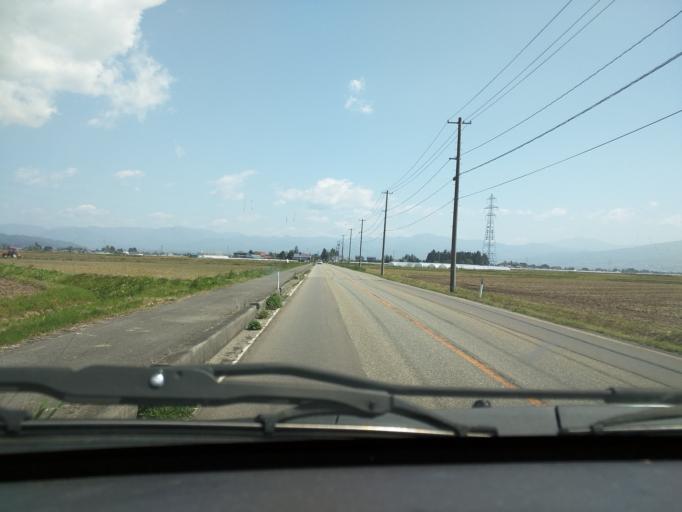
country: JP
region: Fukushima
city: Kitakata
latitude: 37.5734
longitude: 139.8296
